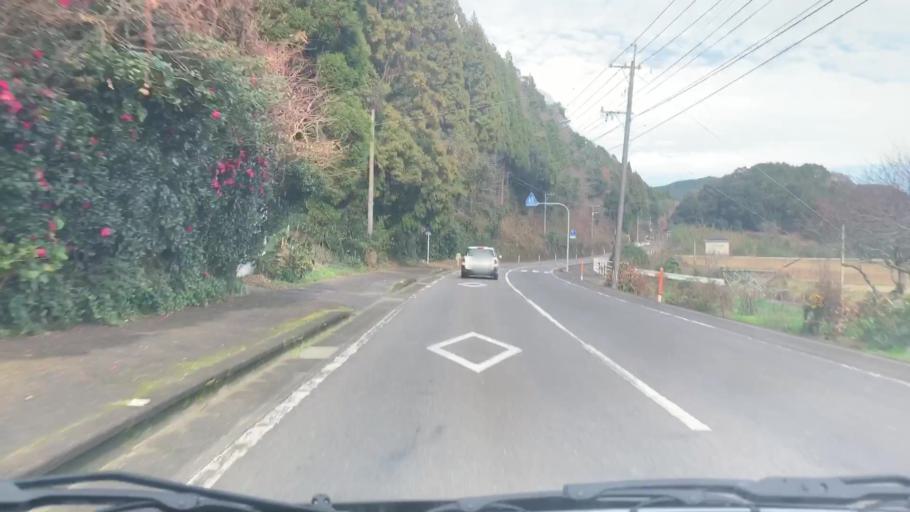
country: JP
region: Saga Prefecture
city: Imaricho-ko
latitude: 33.3161
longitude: 129.9699
